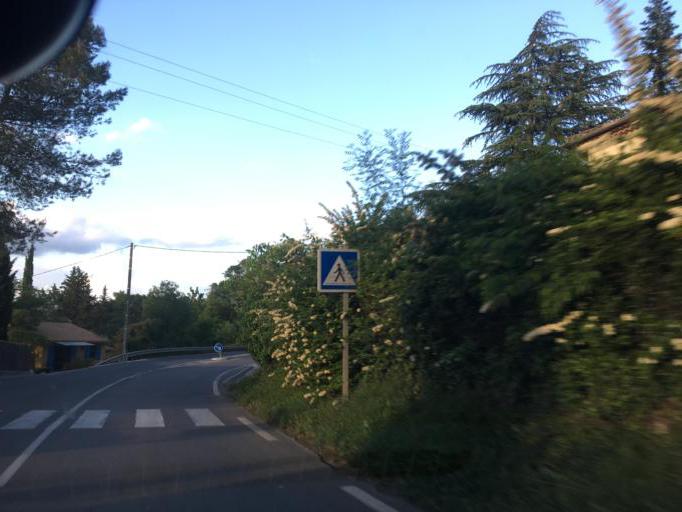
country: FR
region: Provence-Alpes-Cote d'Azur
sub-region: Departement du Var
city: Carces
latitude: 43.4735
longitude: 6.1746
